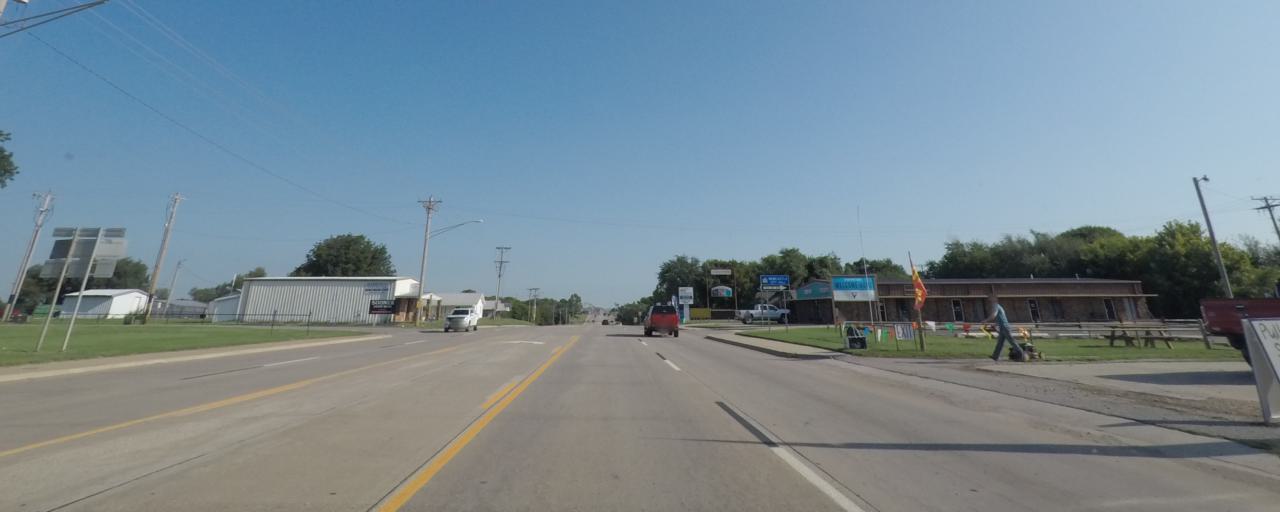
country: US
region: Oklahoma
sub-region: McClain County
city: Newcastle
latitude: 35.2484
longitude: -97.6002
